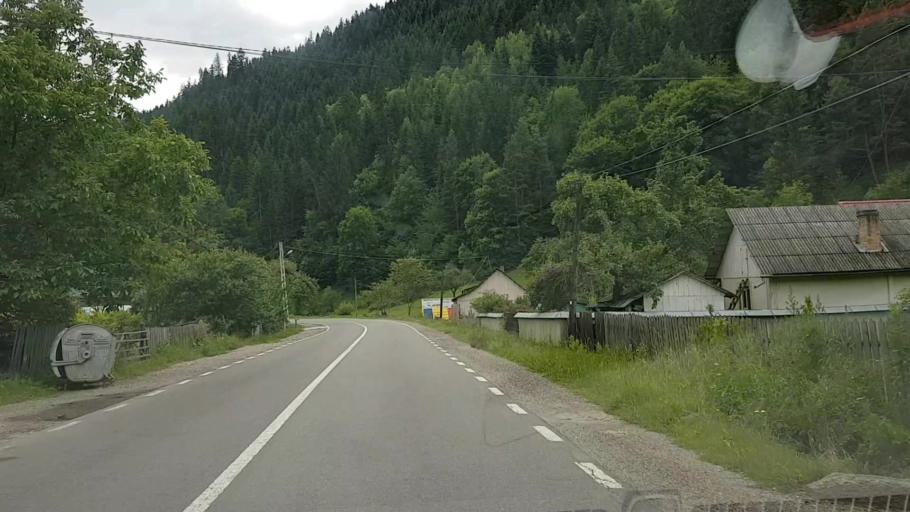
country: RO
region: Neamt
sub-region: Comuna Poiana Teiului
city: Poiana Teiului
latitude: 47.1092
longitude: 25.9316
